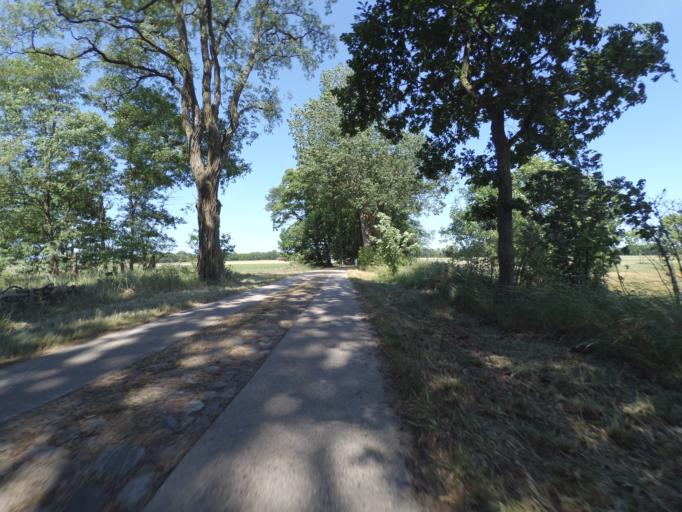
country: DE
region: Brandenburg
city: Heiligengrabe
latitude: 53.2201
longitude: 12.3280
